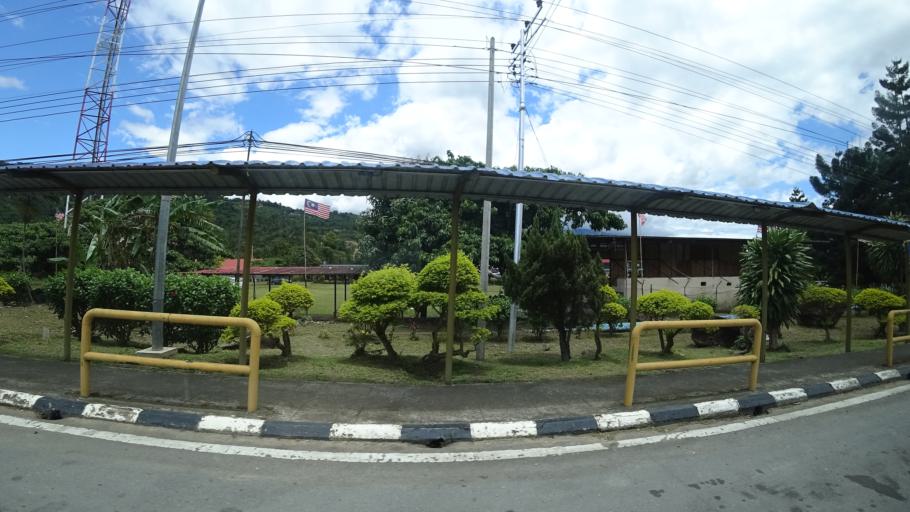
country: MY
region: Sabah
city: Ranau
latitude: 5.9541
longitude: 116.6623
